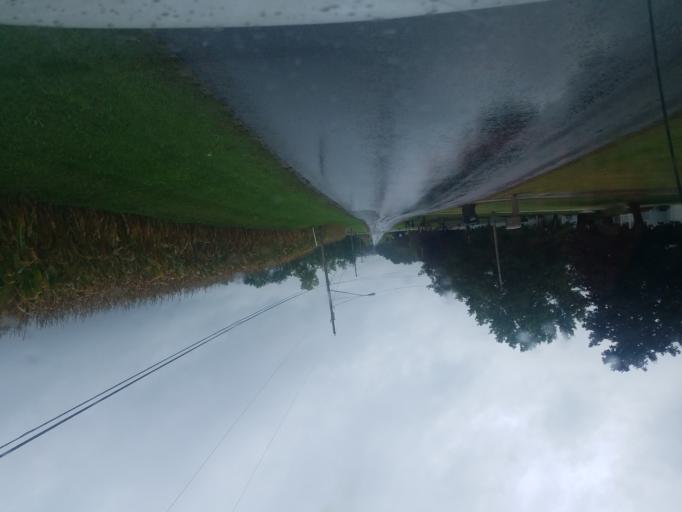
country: US
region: Ohio
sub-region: Wayne County
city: Creston
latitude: 40.9764
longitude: -81.9093
